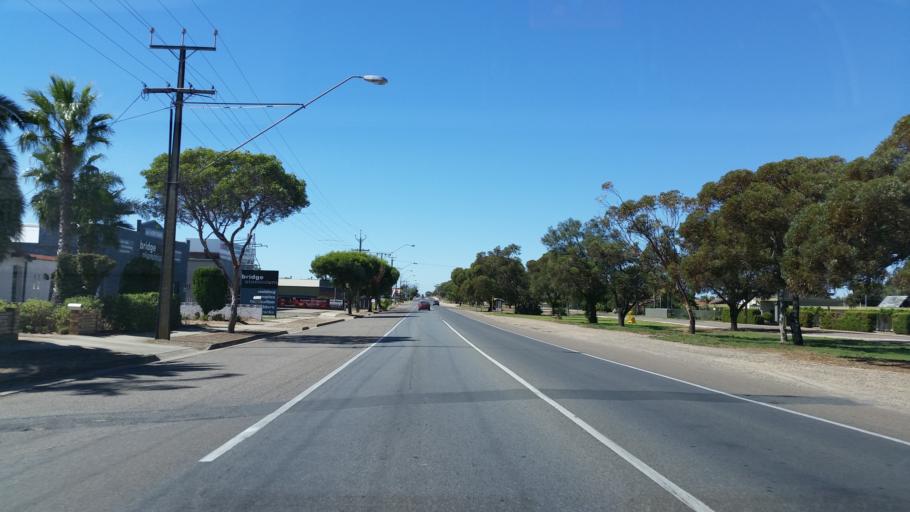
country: AU
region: South Australia
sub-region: Murray Bridge
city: Murray Bridge
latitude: -35.1317
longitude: 139.2448
